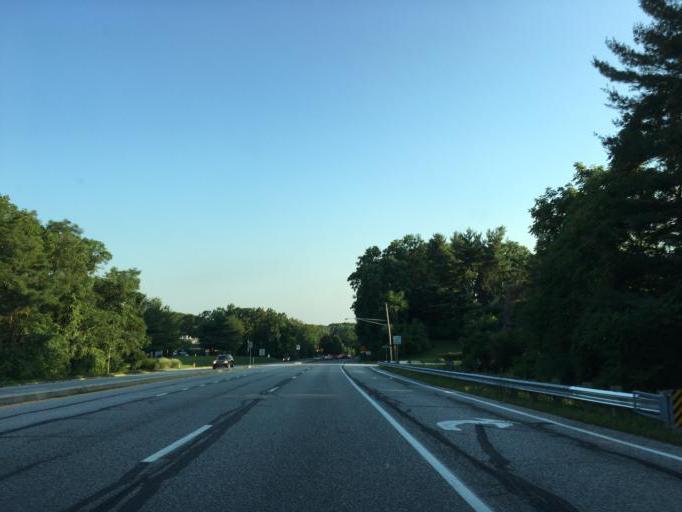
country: US
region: Maryland
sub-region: Baltimore County
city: Lutherville
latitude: 39.4091
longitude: -76.6314
